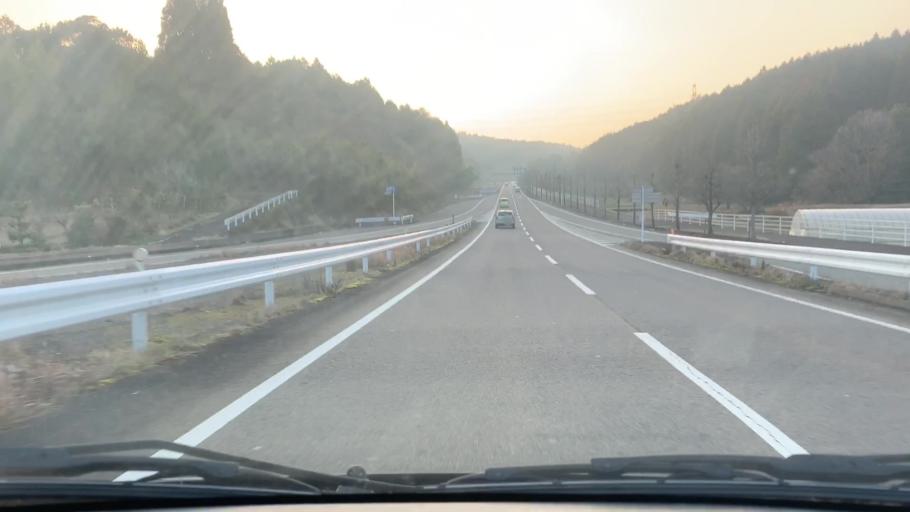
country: JP
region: Saga Prefecture
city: Imaricho-ko
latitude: 33.2602
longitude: 129.9305
